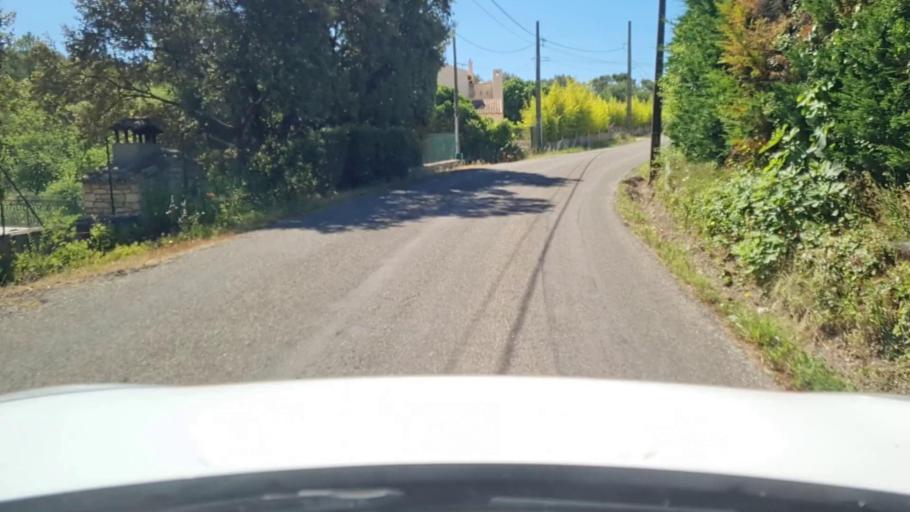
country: FR
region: Languedoc-Roussillon
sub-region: Departement du Gard
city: Villevieille
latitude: 43.7757
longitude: 4.1218
